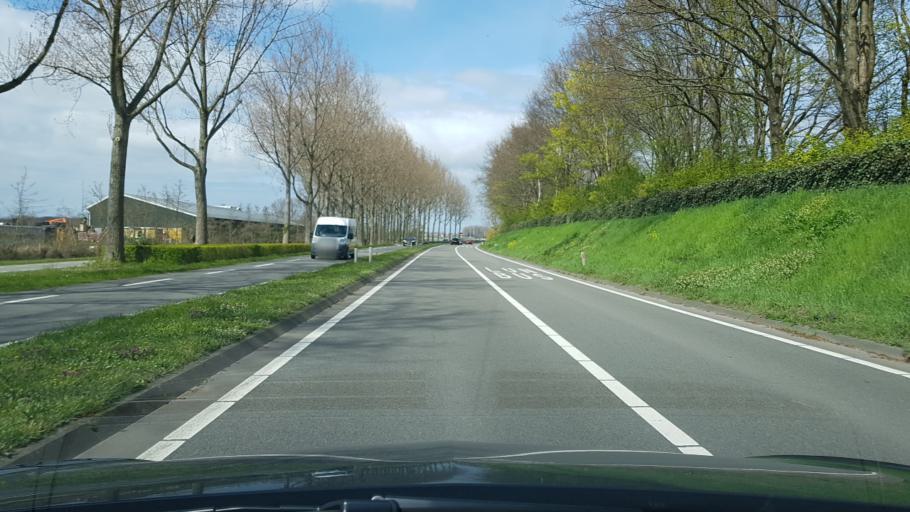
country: NL
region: South Holland
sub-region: Gemeente Leiden
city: Leiden
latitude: 52.1153
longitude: 4.4936
